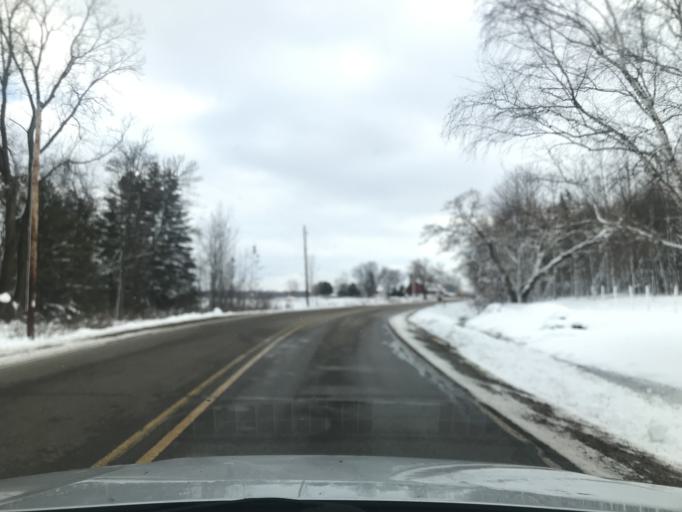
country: US
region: Wisconsin
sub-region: Oconto County
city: Oconto
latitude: 44.9436
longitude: -87.9869
